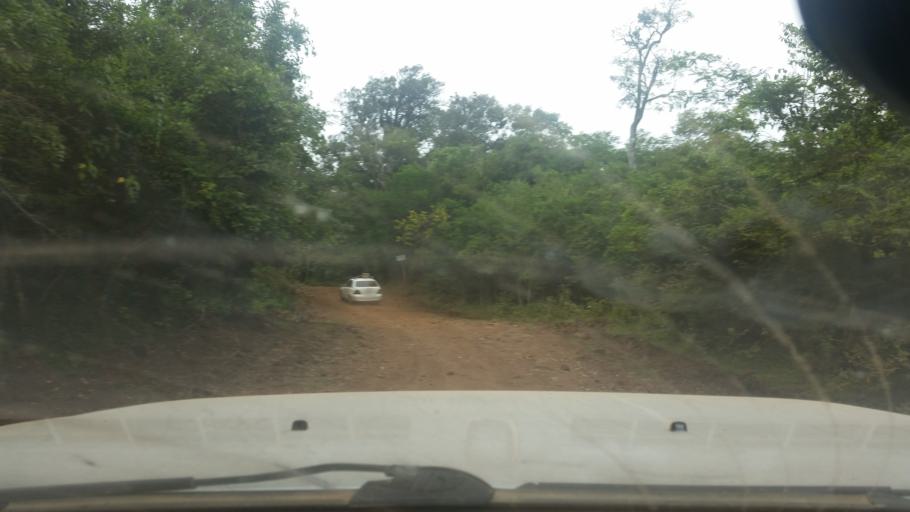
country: PY
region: Guaira
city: Independencia
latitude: -25.8184
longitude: -56.2769
